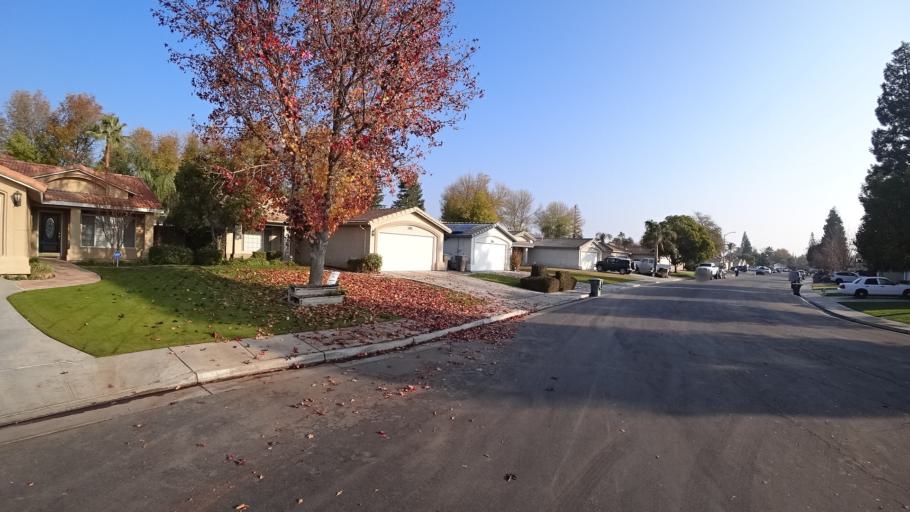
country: US
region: California
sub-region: Kern County
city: Greenacres
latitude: 35.3246
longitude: -119.0951
